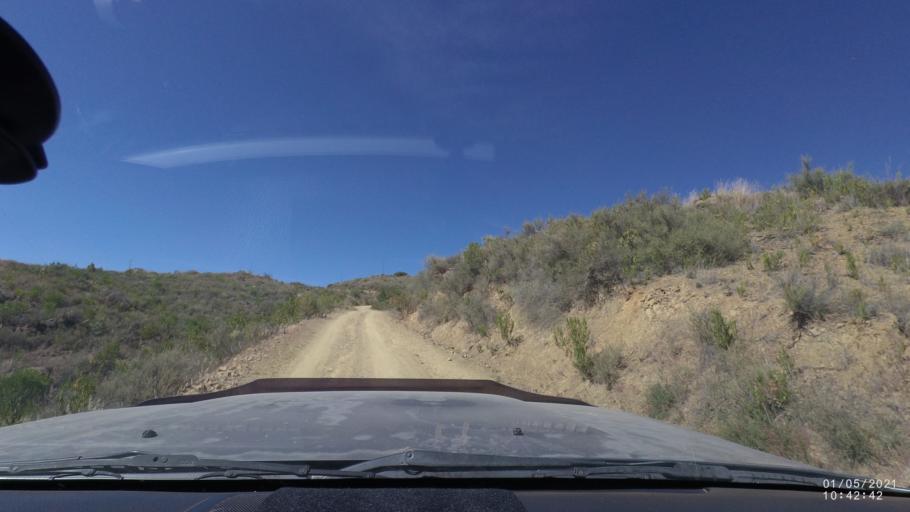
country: BO
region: Cochabamba
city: Capinota
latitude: -17.6130
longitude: -66.1761
